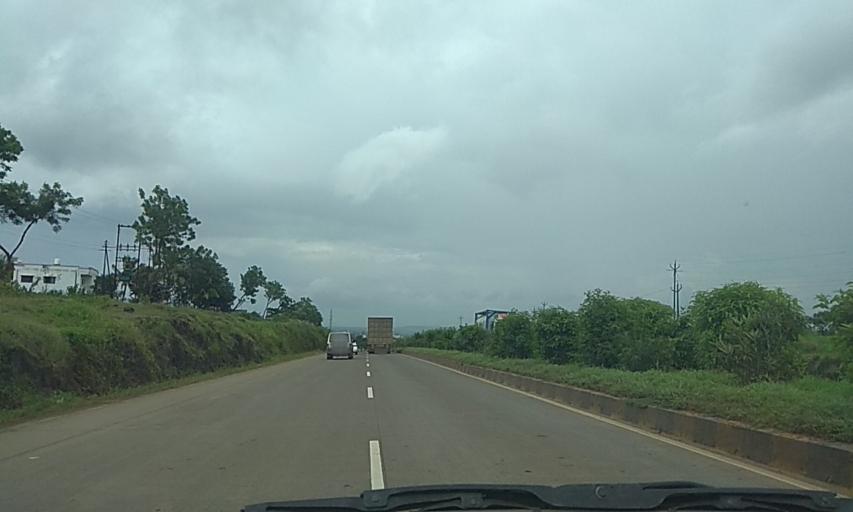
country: IN
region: Maharashtra
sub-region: Kolhapur
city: Kolhapur
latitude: 16.6752
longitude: 74.2702
